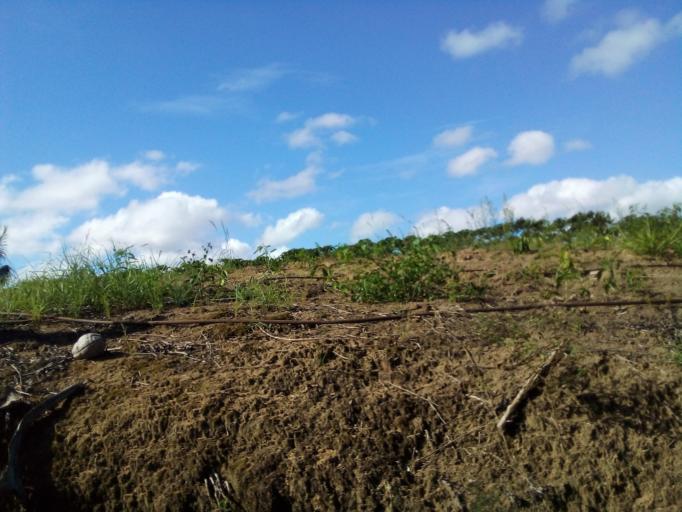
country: BR
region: Espirito Santo
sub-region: Aracruz
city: Aracruz
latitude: -19.7132
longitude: -40.2096
